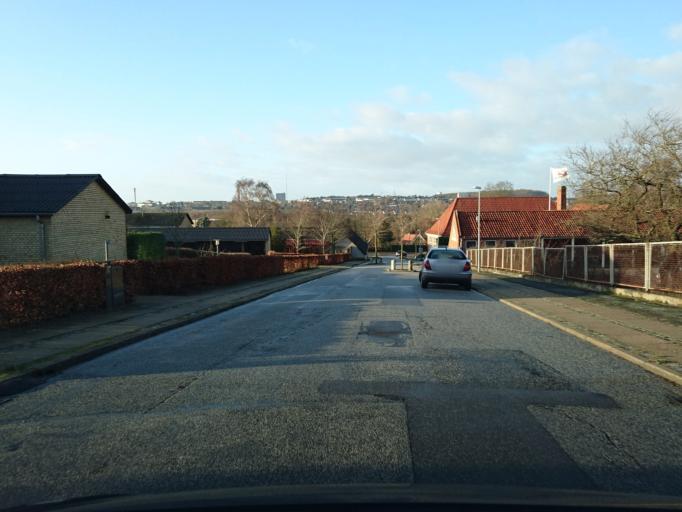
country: DK
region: North Denmark
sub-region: Alborg Kommune
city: Aalborg
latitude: 57.0242
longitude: 9.9295
